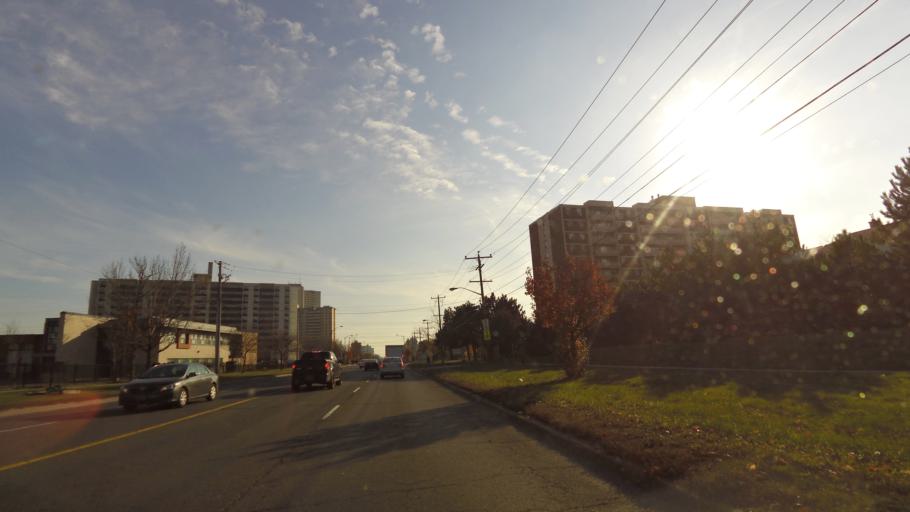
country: CA
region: Ontario
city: Concord
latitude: 43.7631
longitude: -79.5194
